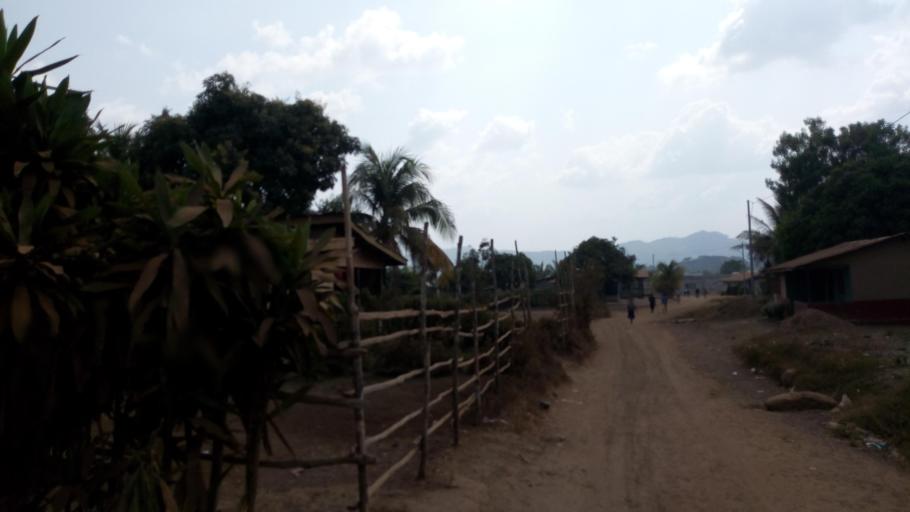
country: SL
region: Southern Province
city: Mogbwemo
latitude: 7.7808
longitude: -12.3000
